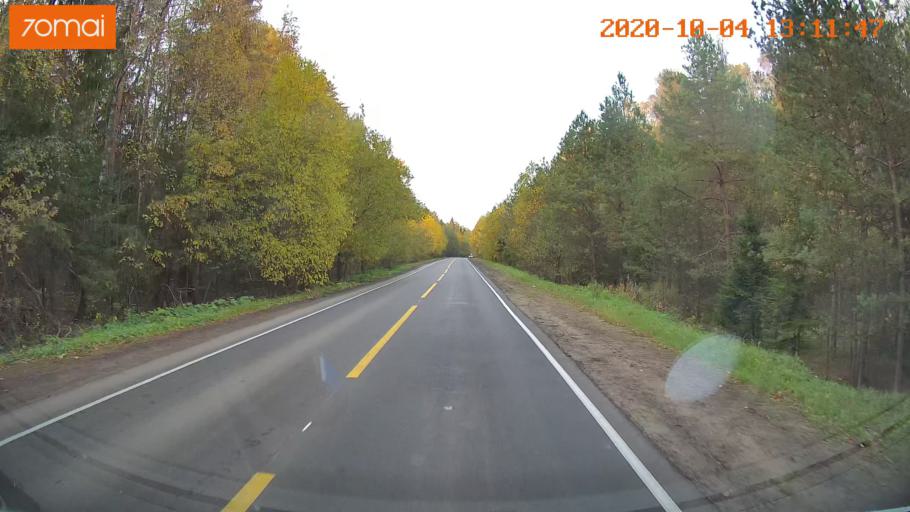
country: RU
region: Ivanovo
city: Bogorodskoye
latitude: 57.0791
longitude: 40.9383
